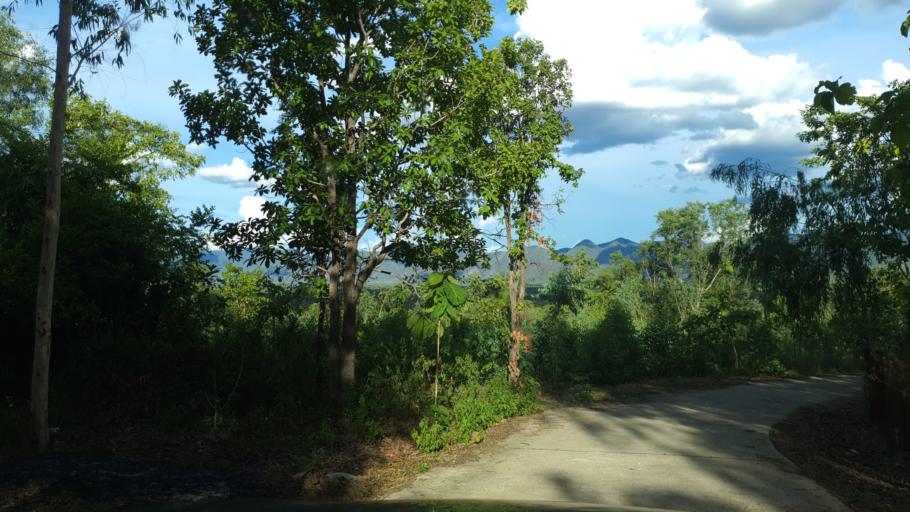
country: TH
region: Lampang
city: Sop Prap
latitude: 17.8795
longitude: 99.2974
